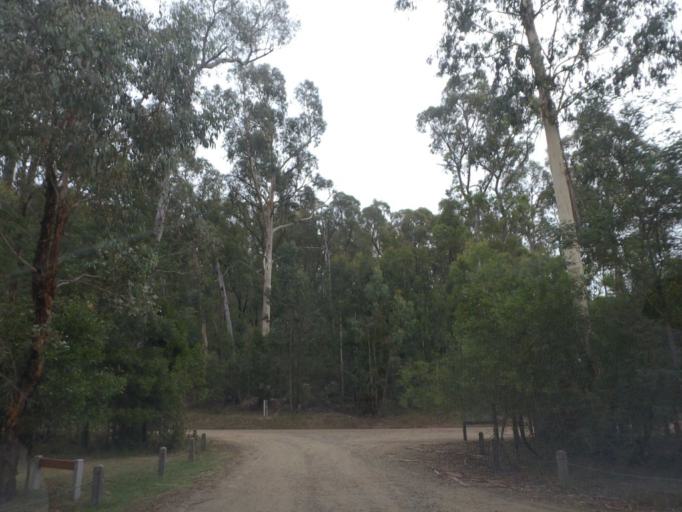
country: AU
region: Victoria
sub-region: Murrindindi
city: Alexandra
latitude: -37.3890
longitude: 145.5530
